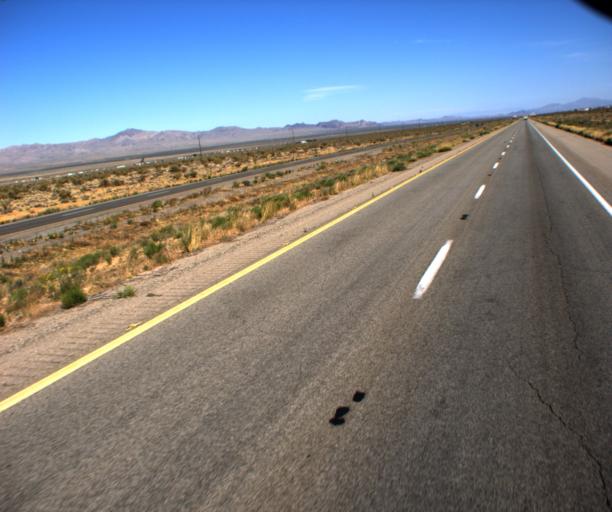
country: US
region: Arizona
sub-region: Mohave County
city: Dolan Springs
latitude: 35.5044
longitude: -114.3347
